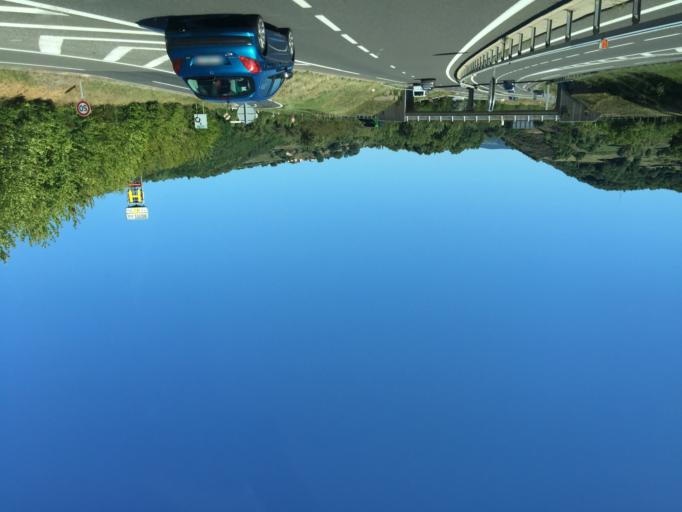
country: FR
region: Languedoc-Roussillon
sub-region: Departement de la Lozere
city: La Canourgue
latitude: 44.4365
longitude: 3.1956
